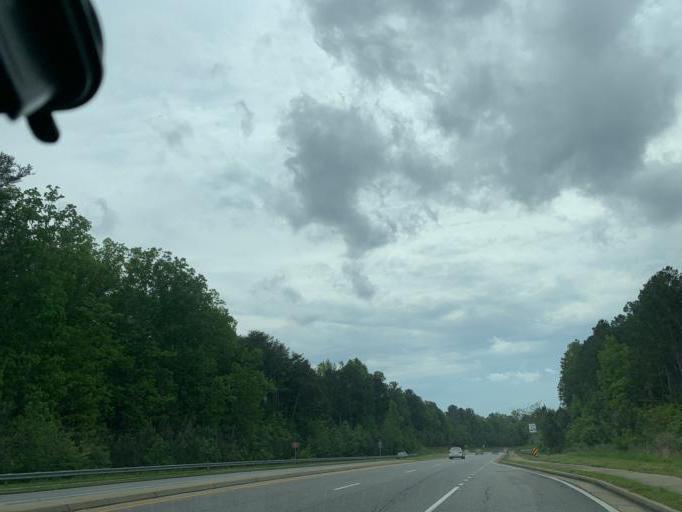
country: US
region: Georgia
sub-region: Forsyth County
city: Cumming
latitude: 34.2063
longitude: -84.1181
